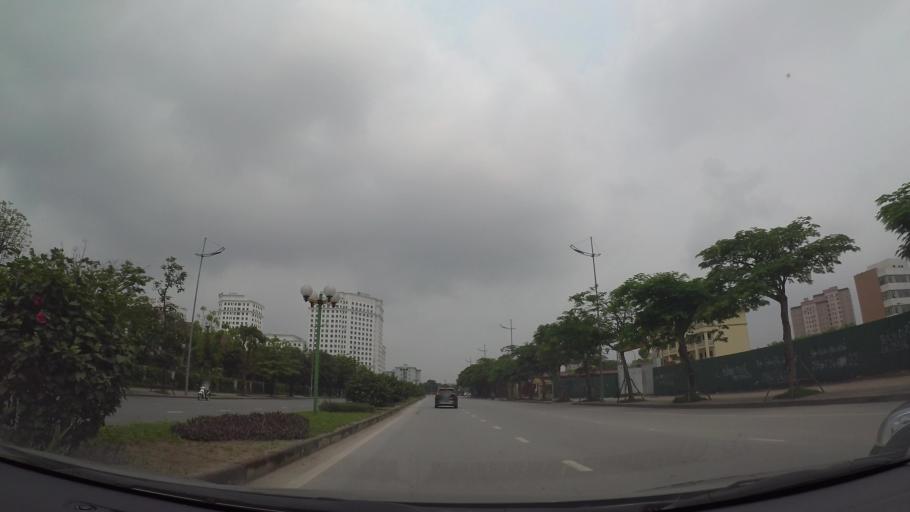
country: VN
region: Ha Noi
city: Trau Quy
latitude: 21.0547
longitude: 105.9153
